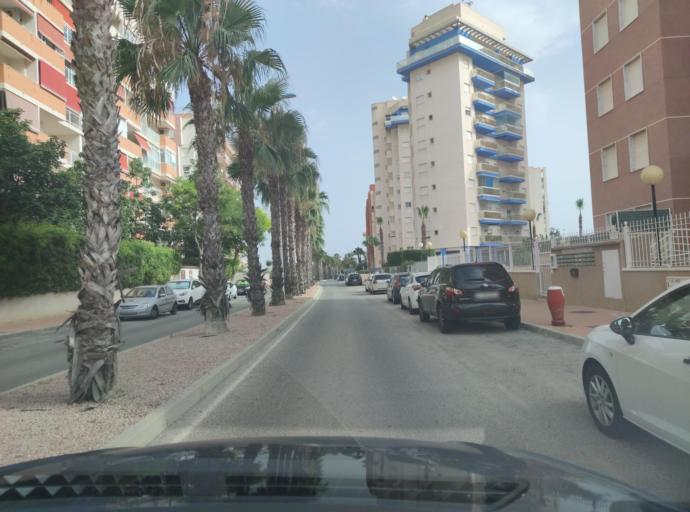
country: ES
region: Valencia
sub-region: Provincia de Alicante
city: Guardamar del Segura
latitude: 38.1005
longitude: -0.6556
